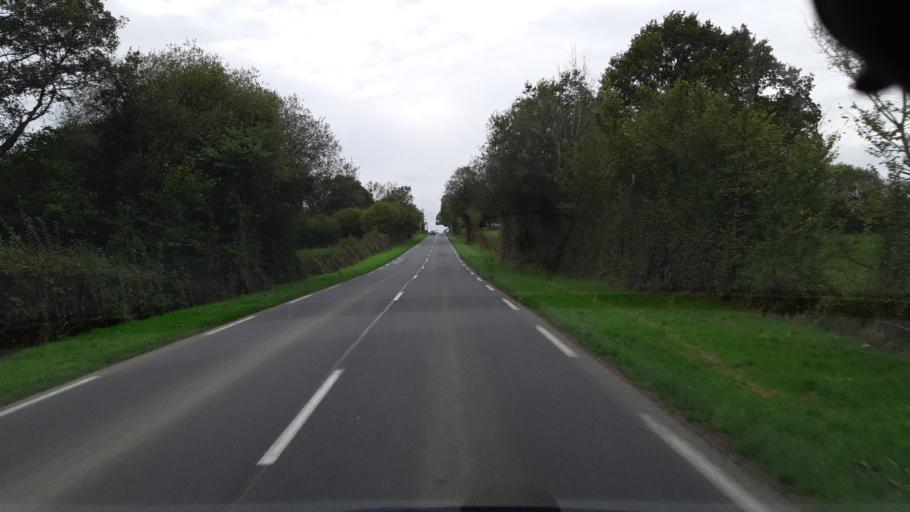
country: FR
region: Lower Normandy
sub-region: Departement de la Manche
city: Hambye
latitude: 48.9450
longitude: -1.2903
